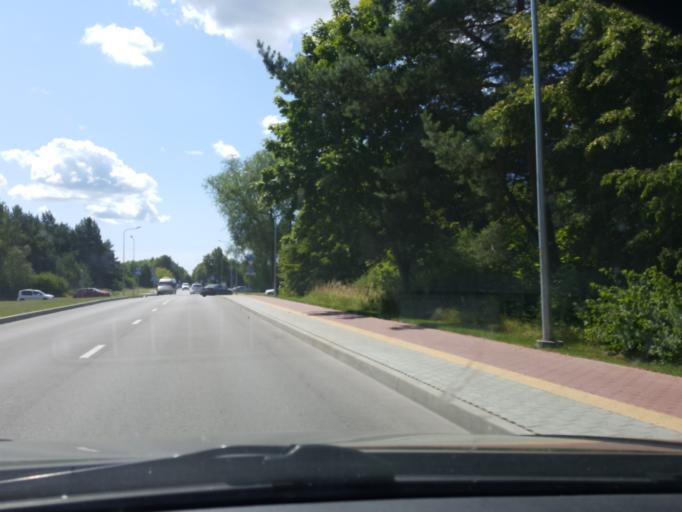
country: LT
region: Klaipedos apskritis
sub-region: Klaipeda
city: Palanga
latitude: 55.9372
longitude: 21.0788
